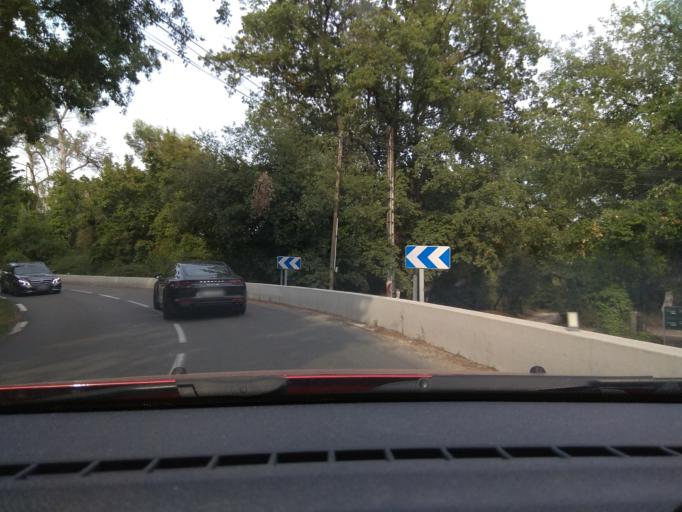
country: FR
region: Provence-Alpes-Cote d'Azur
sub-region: Departement des Alpes-Maritimes
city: Le Rouret
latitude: 43.6509
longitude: 7.0268
